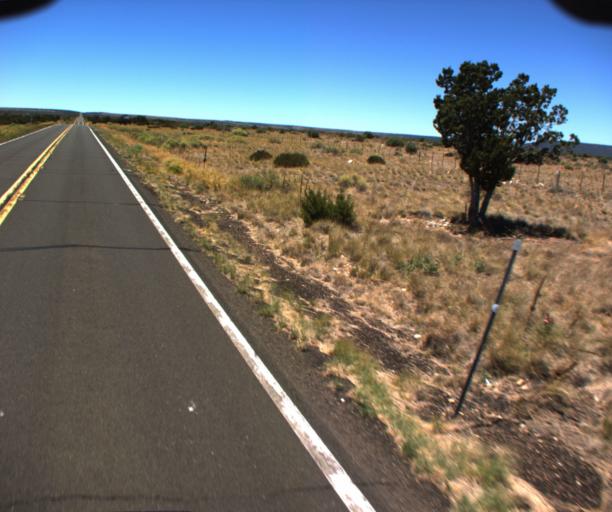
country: US
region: Arizona
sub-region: Coconino County
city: LeChee
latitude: 34.7634
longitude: -111.0173
